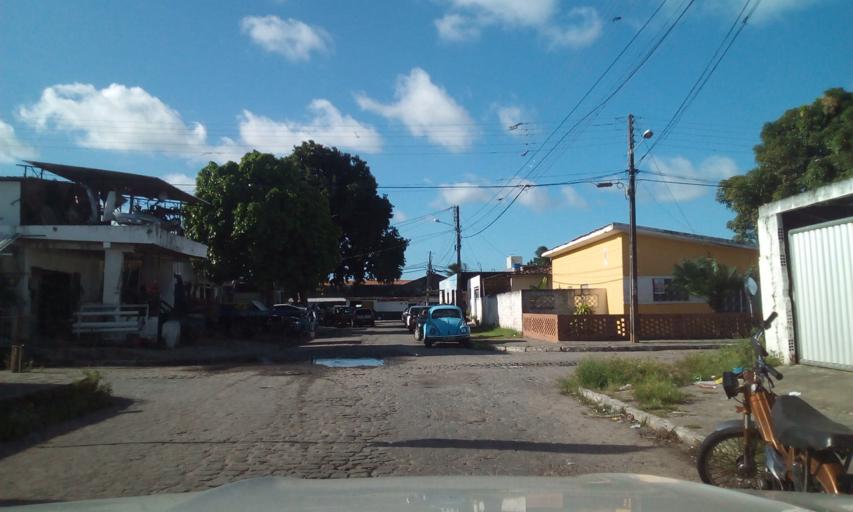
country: BR
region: Paraiba
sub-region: Bayeux
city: Bayeux
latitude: -7.1514
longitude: -34.8934
